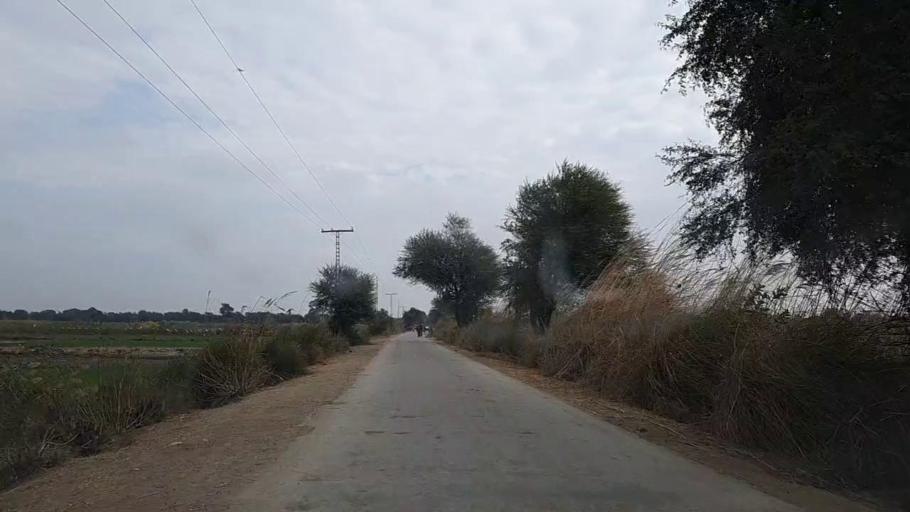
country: PK
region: Sindh
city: Sanghar
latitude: 26.2302
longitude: 68.9934
